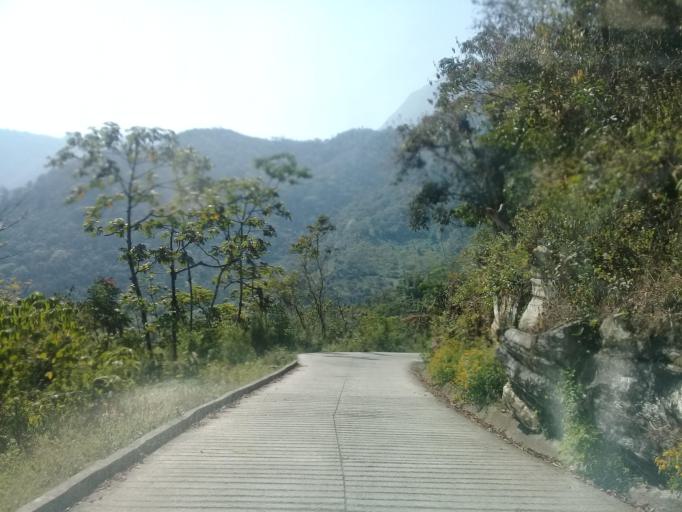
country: MX
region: Veracruz
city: Rafael Delgado
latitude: 18.7826
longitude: -97.0251
